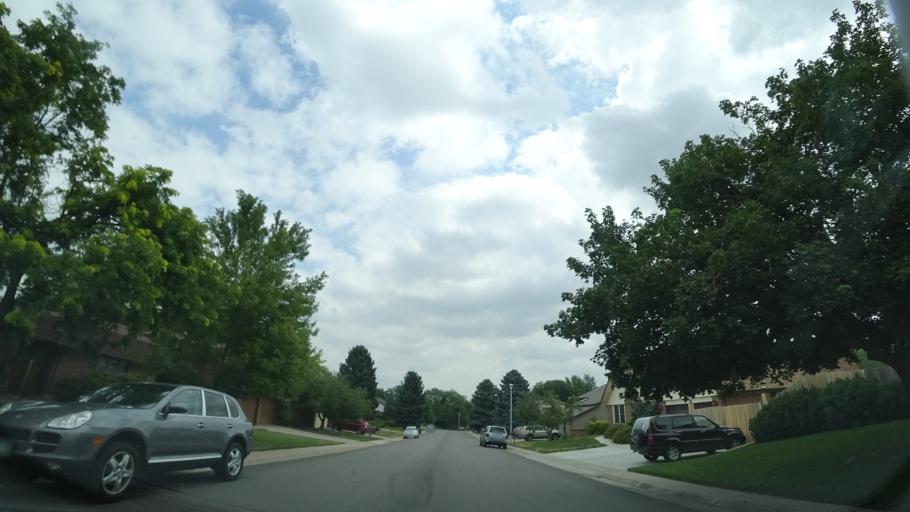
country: US
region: Colorado
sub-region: Jefferson County
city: West Pleasant View
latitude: 39.7195
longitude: -105.1576
